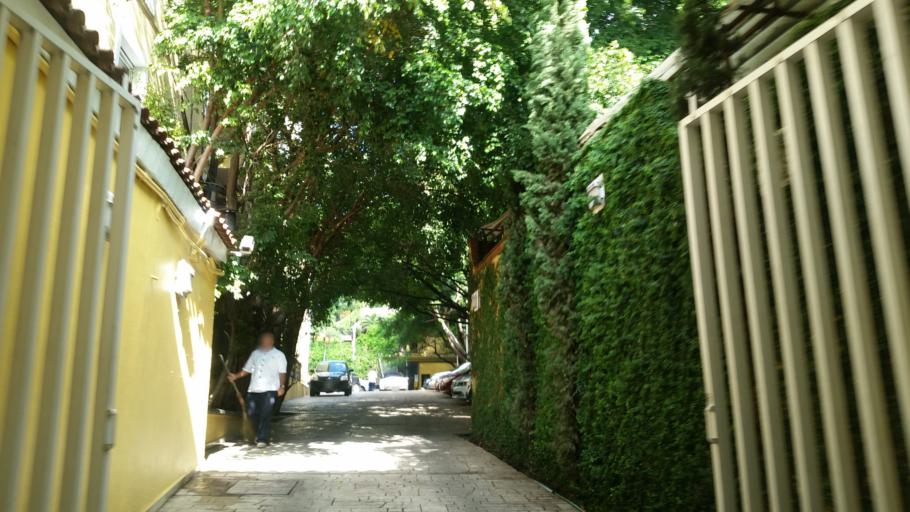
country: MX
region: Morelos
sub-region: Cuernavaca
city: Cuernavaca
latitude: 18.9111
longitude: -99.2214
